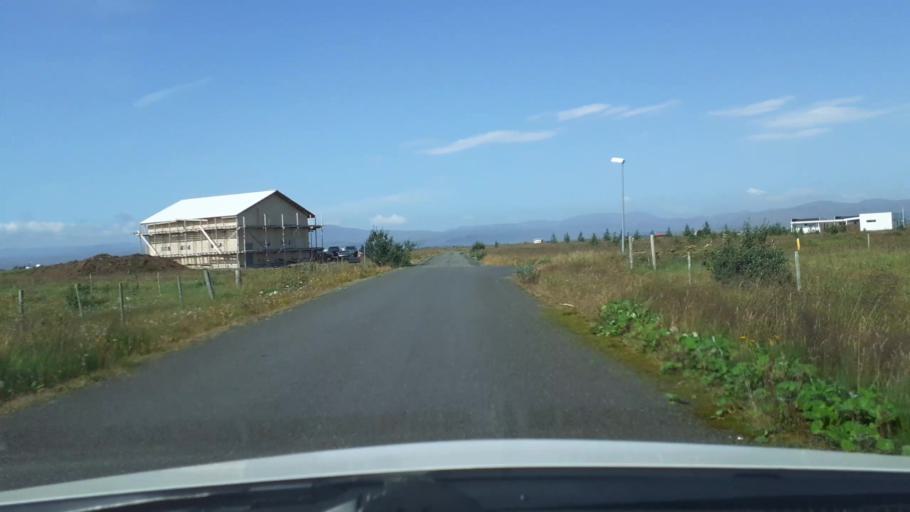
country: IS
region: South
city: Selfoss
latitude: 63.8969
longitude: -21.0823
